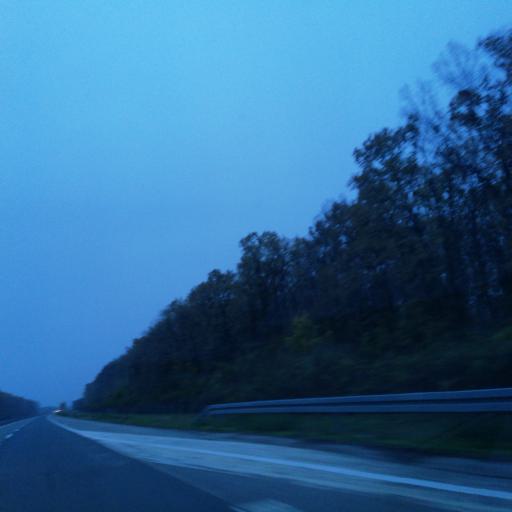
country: RS
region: Autonomna Pokrajina Vojvodina
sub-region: Sremski Okrug
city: Sid
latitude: 45.0465
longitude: 19.2318
